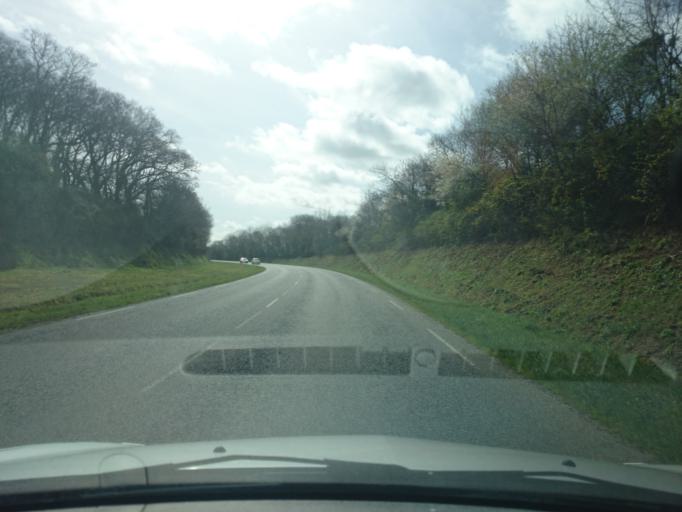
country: FR
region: Brittany
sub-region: Departement du Finistere
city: Gouesnou
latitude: 48.4405
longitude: -4.4569
